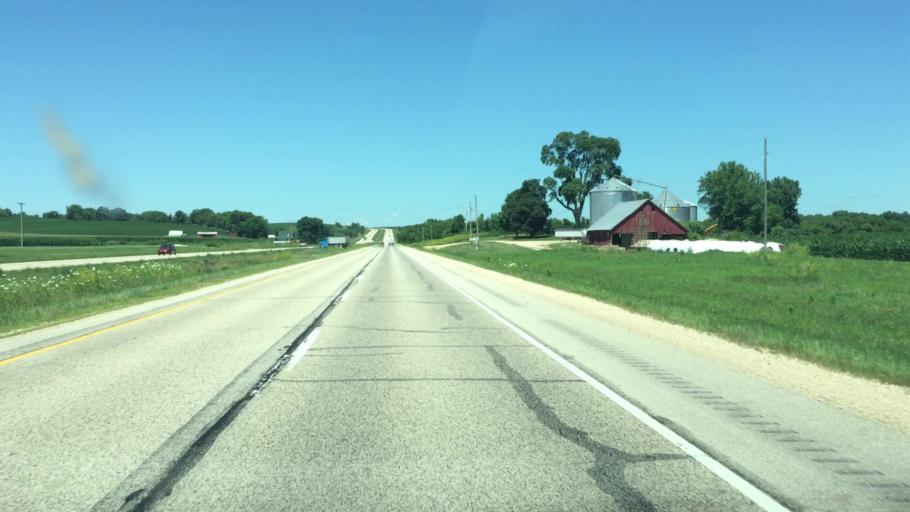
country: US
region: Iowa
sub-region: Jackson County
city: Maquoketa
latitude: 42.1766
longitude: -90.6728
